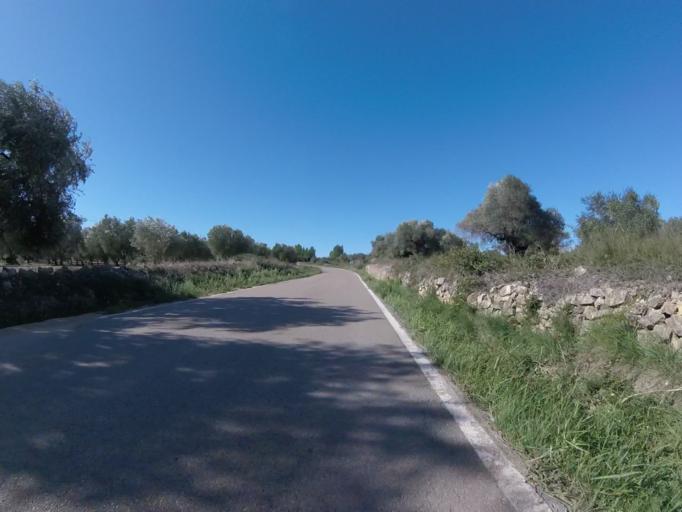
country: ES
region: Valencia
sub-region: Provincia de Castello
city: Chert/Xert
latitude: 40.4592
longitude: 0.1532
